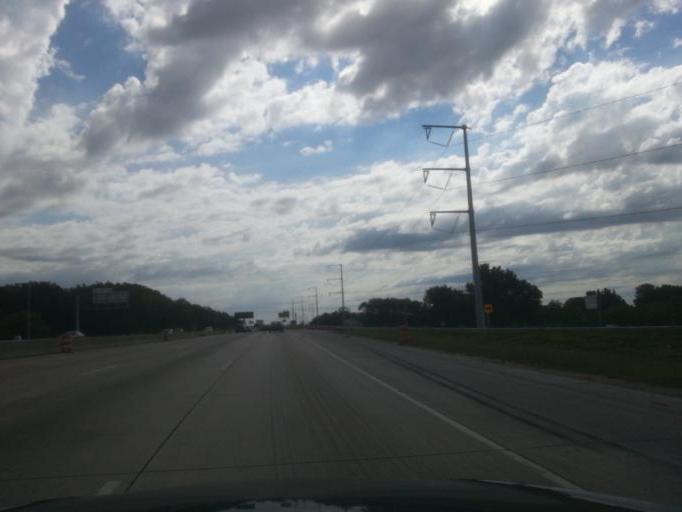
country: US
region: Wisconsin
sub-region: Dane County
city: Monona
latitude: 43.0434
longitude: -89.3685
